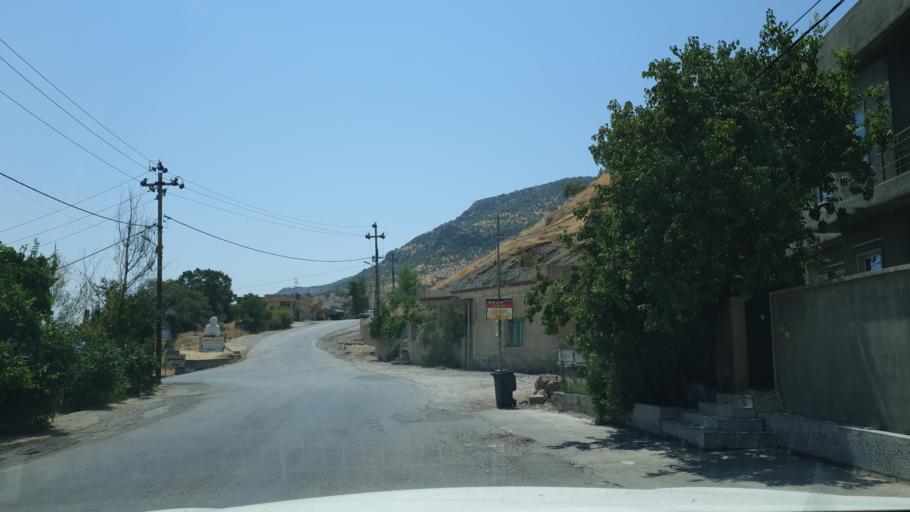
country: IQ
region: Arbil
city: Nahiyat Hiran
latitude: 36.2824
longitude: 44.4923
